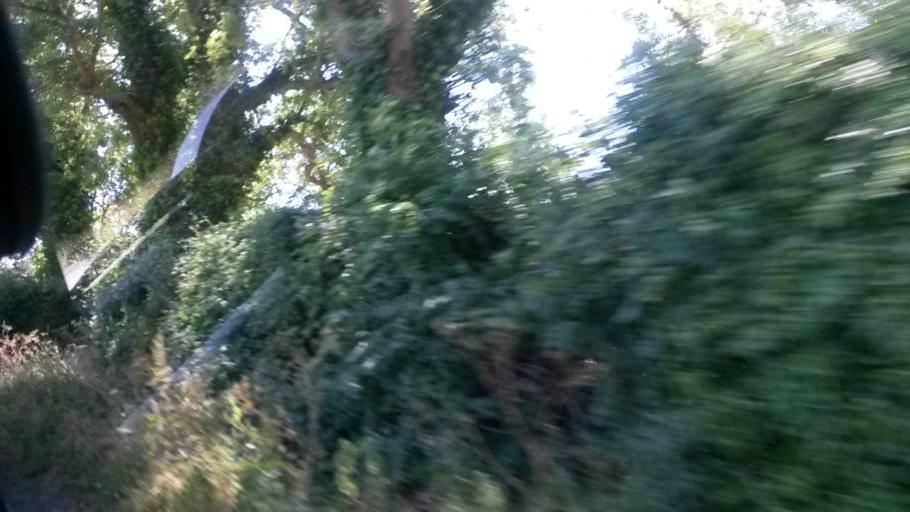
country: IE
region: Leinster
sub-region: Fingal County
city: Swords
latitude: 53.5220
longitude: -6.2358
